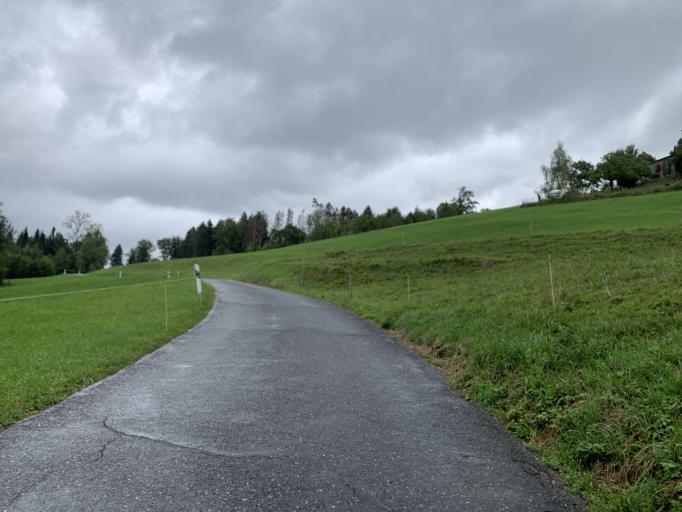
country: CH
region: Zurich
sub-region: Bezirk Hinwil
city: Hadlikon
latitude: 47.3021
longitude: 8.8582
